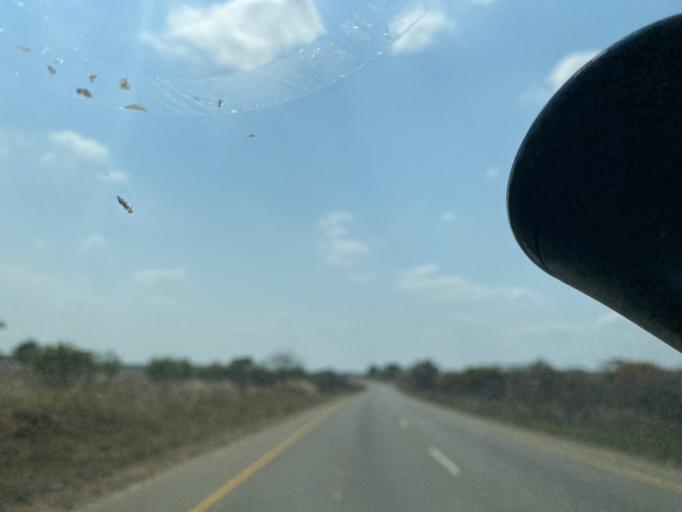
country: ZM
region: Lusaka
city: Chongwe
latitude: -15.5450
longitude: 28.6663
